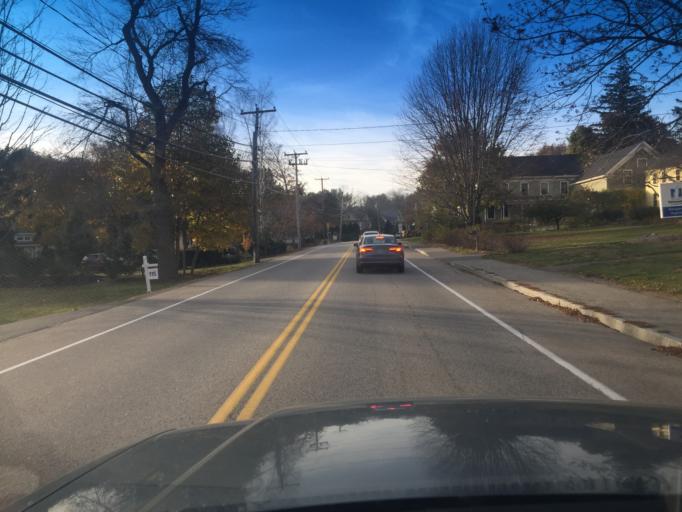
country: US
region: Maine
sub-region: York County
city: York Harbor
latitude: 43.1460
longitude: -70.6578
